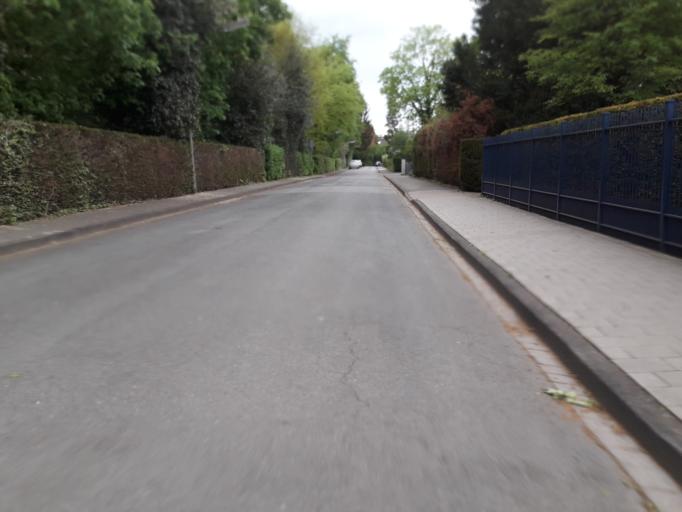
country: DE
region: North Rhine-Westphalia
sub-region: Regierungsbezirk Munster
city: Muenster
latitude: 51.9009
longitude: 7.6460
